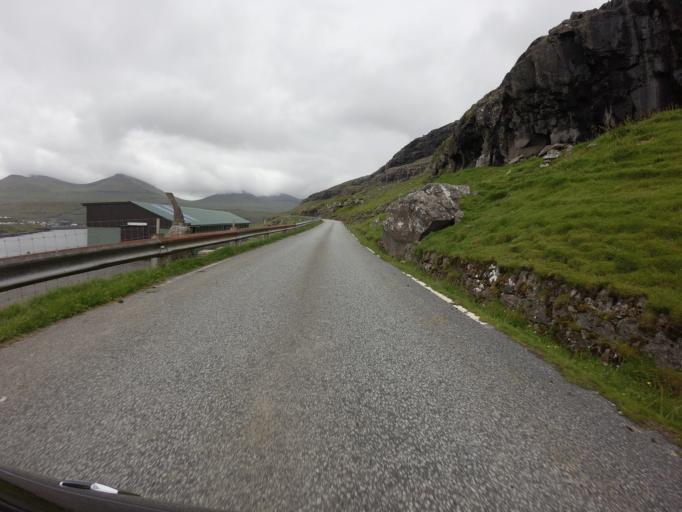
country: FO
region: Eysturoy
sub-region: Eidi
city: Eidi
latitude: 62.2948
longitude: -7.1276
